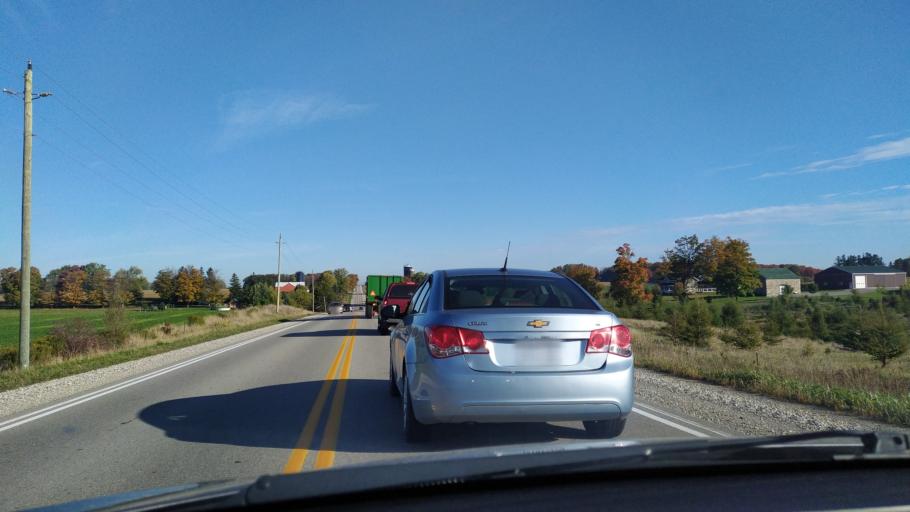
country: CA
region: Ontario
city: Stratford
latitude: 43.4582
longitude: -80.8390
